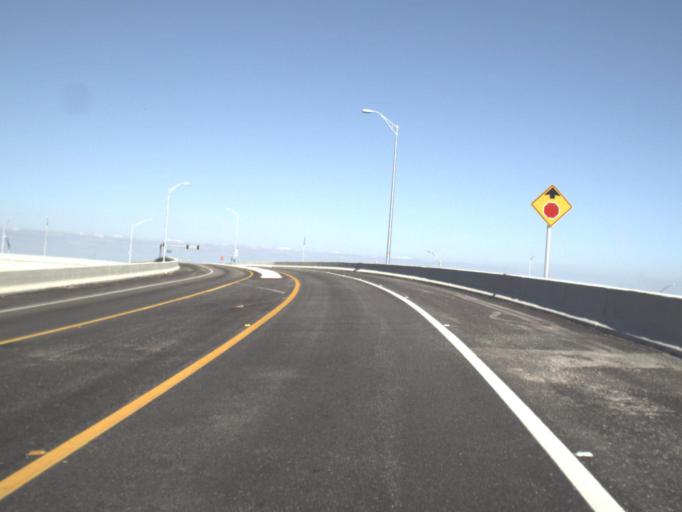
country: US
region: Florida
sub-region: Glades County
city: Moore Haven
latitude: 26.7539
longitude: -81.0828
